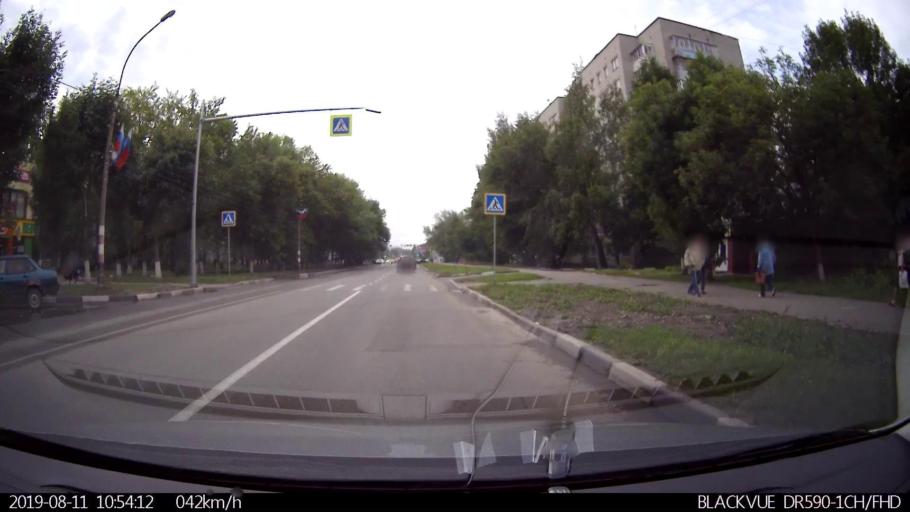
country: RU
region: Ulyanovsk
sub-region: Ulyanovskiy Rayon
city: Ulyanovsk
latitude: 54.2576
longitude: 48.3342
